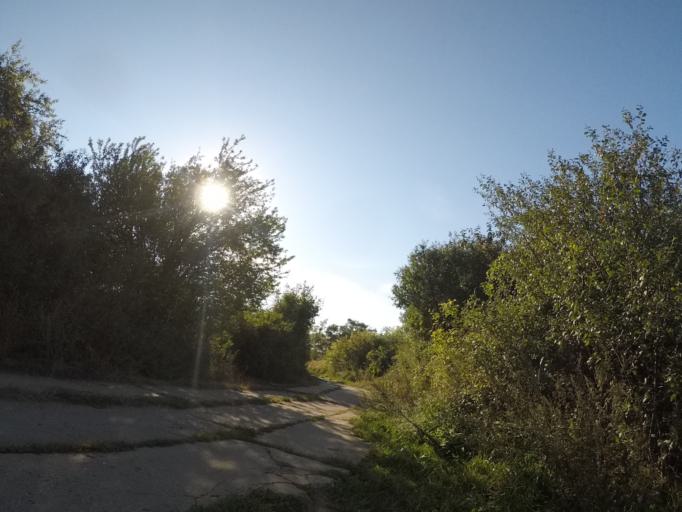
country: SK
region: Kosicky
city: Kosice
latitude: 48.7218
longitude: 21.2040
